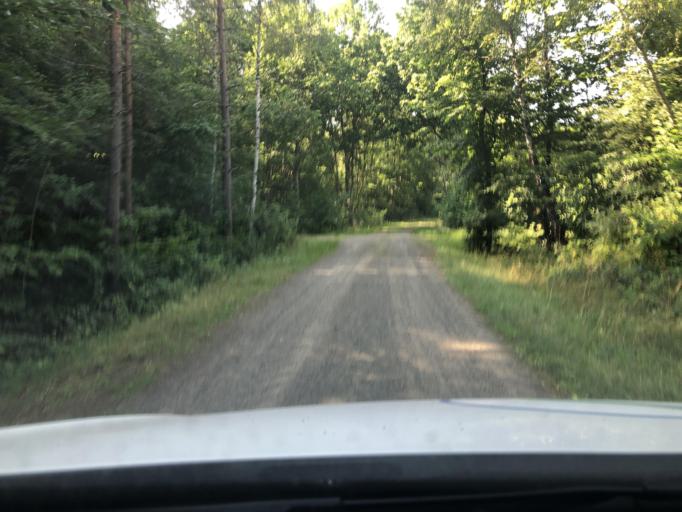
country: SE
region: Skane
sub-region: Kristianstads Kommun
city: Degeberga
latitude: 55.8029
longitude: 14.1395
